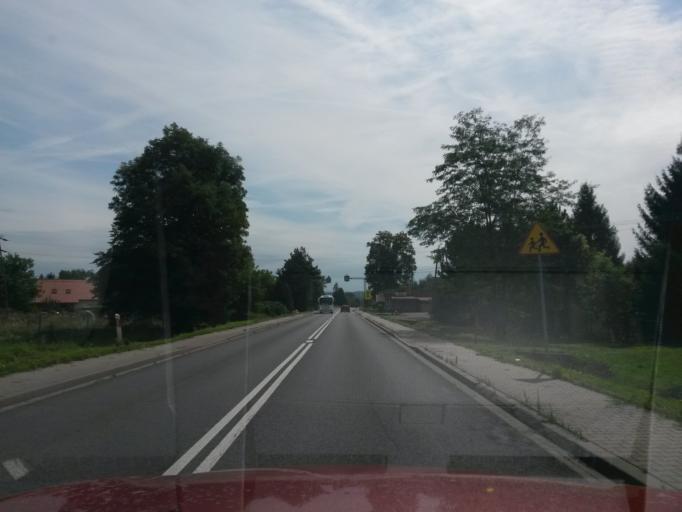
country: PL
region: Lesser Poland Voivodeship
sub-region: Powiat wielicki
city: Targowisko
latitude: 49.9808
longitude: 20.2900
